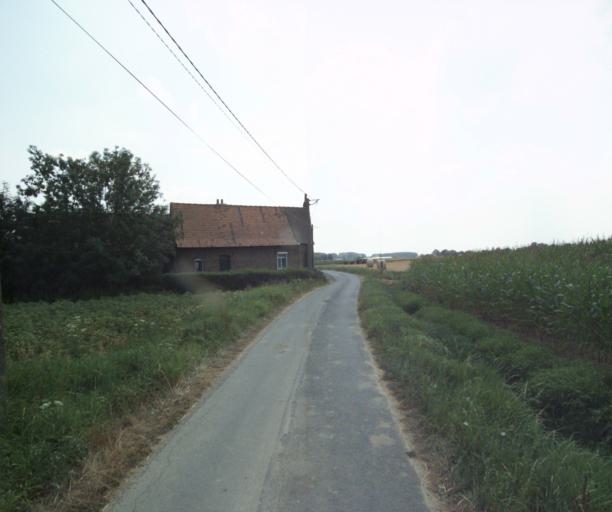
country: FR
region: Nord-Pas-de-Calais
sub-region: Departement du Nord
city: Wambrechies
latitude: 50.7185
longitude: 3.0407
